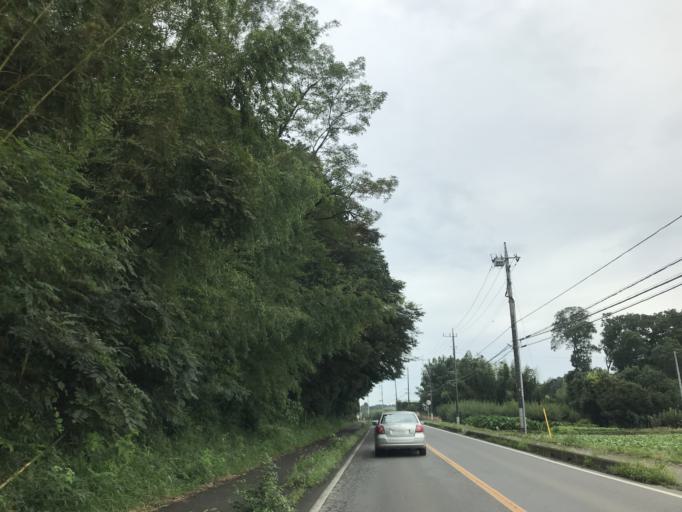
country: JP
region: Ibaraki
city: Sakai
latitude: 36.1348
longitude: 139.7952
